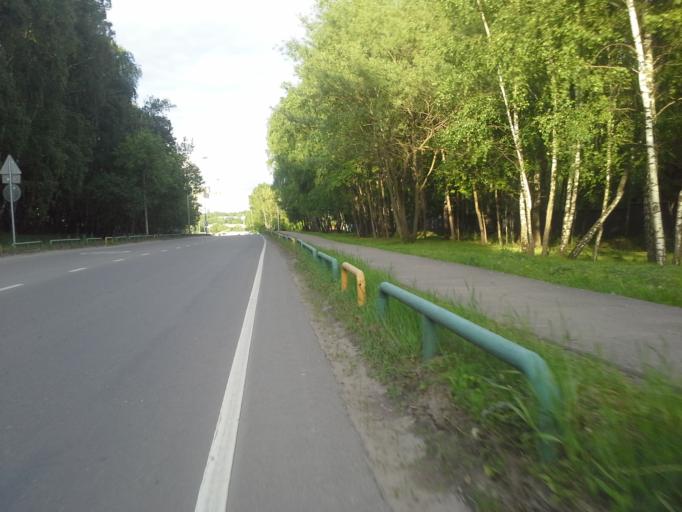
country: RU
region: Moskovskaya
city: Vostryakovo
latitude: 55.6618
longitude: 37.4475
